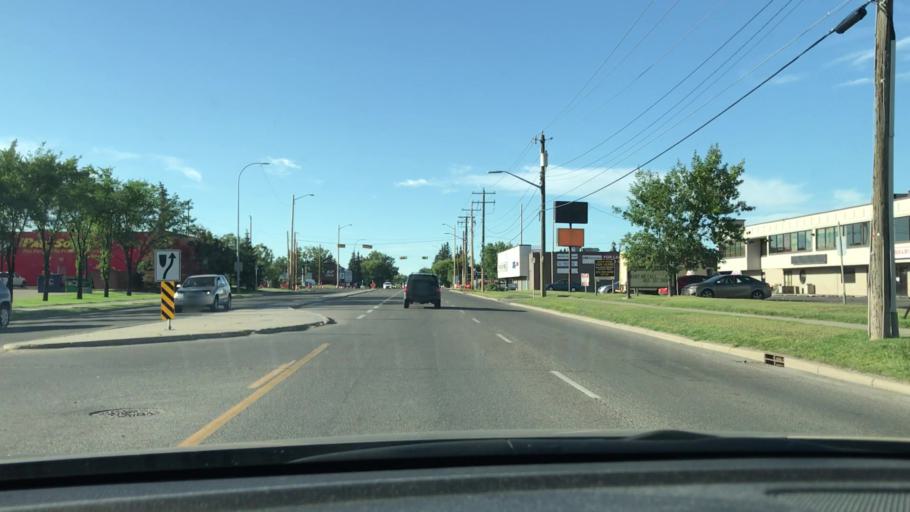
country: CA
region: Alberta
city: Calgary
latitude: 51.0363
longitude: -113.9583
